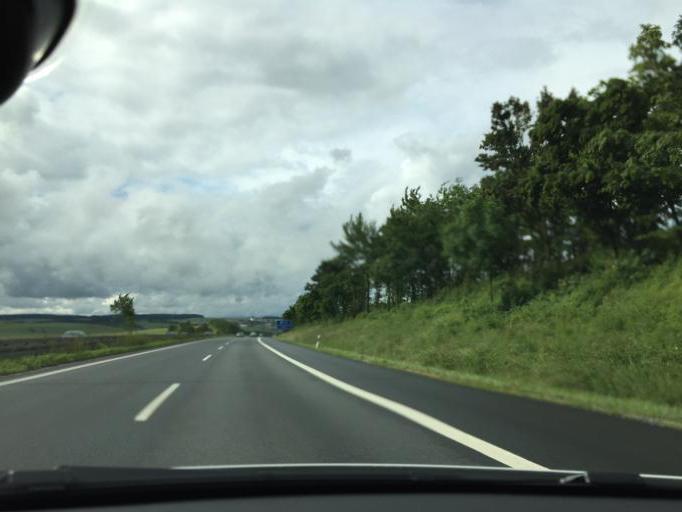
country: DE
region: Bavaria
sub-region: Regierungsbezirk Unterfranken
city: Wasserlosen
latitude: 50.0540
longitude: 10.0538
